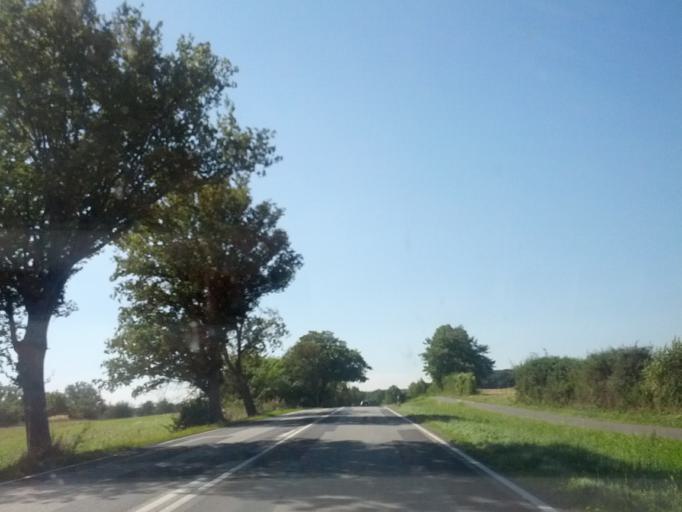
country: DE
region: Mecklenburg-Vorpommern
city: Sagard
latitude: 54.5005
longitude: 13.5265
